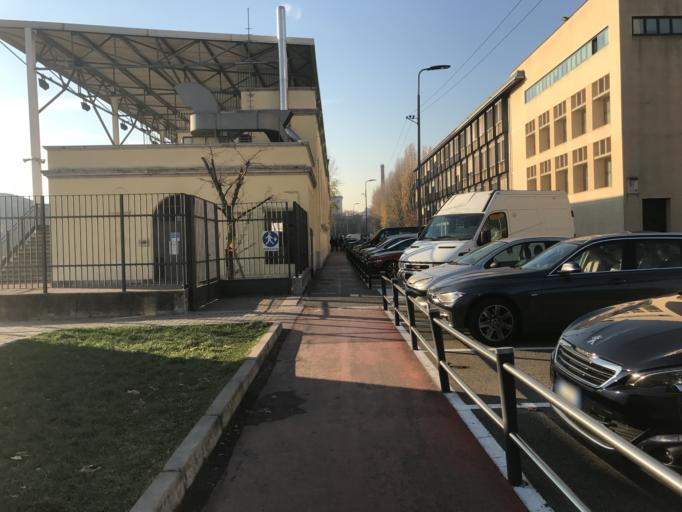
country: IT
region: Lombardy
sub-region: Citta metropolitana di Milano
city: Milano
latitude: 45.4785
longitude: 9.2337
